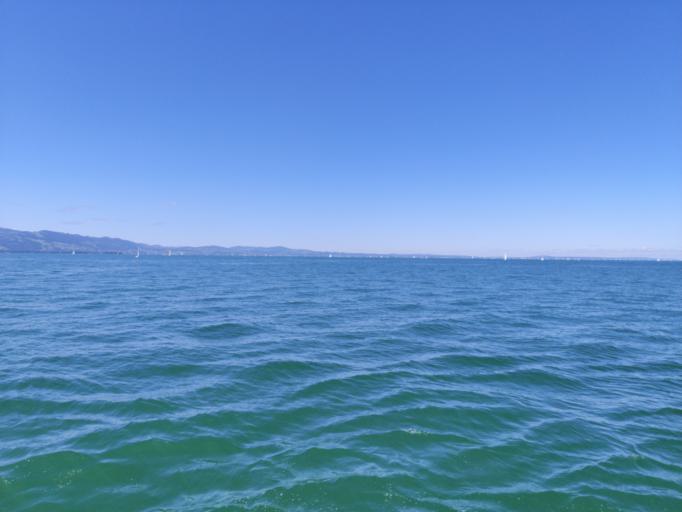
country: DE
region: Bavaria
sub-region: Swabia
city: Bodolz
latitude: 47.5504
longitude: 9.6457
